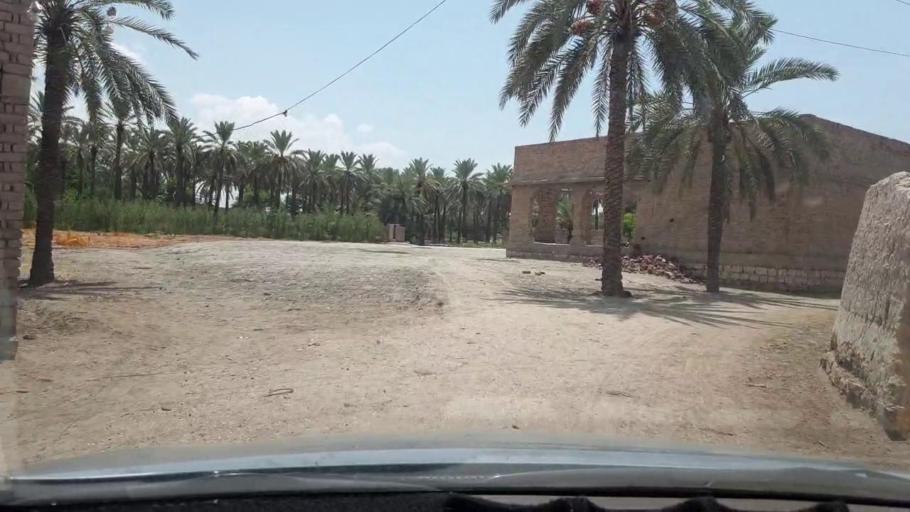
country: PK
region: Sindh
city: Khairpur
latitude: 27.4424
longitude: 68.7918
